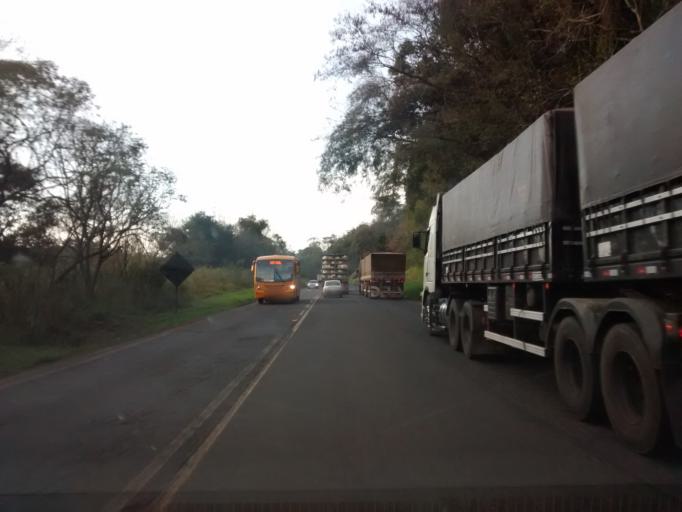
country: BR
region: Parana
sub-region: Francisco Beltrao
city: Francisco Beltrao
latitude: -26.0865
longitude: -53.0687
